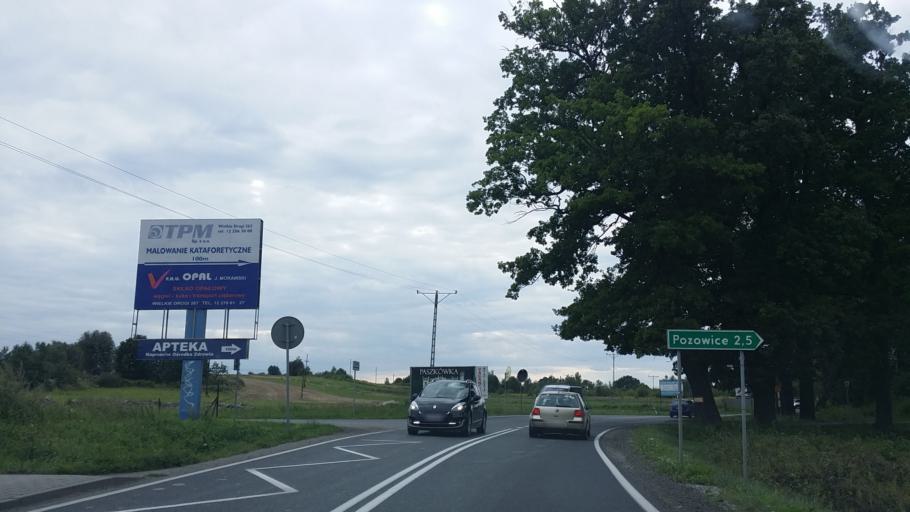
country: PL
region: Lesser Poland Voivodeship
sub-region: Powiat wadowicki
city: Sosnowice
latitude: 49.9590
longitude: 19.7022
